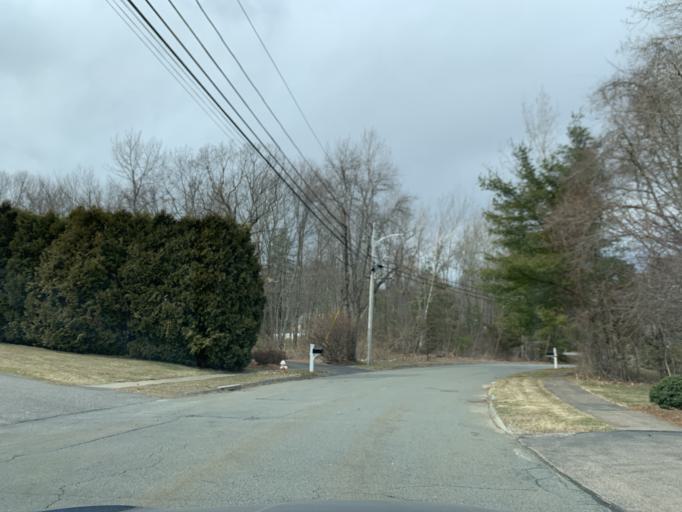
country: US
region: Massachusetts
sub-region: Norfolk County
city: Bellingham
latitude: 42.0430
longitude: -71.4458
